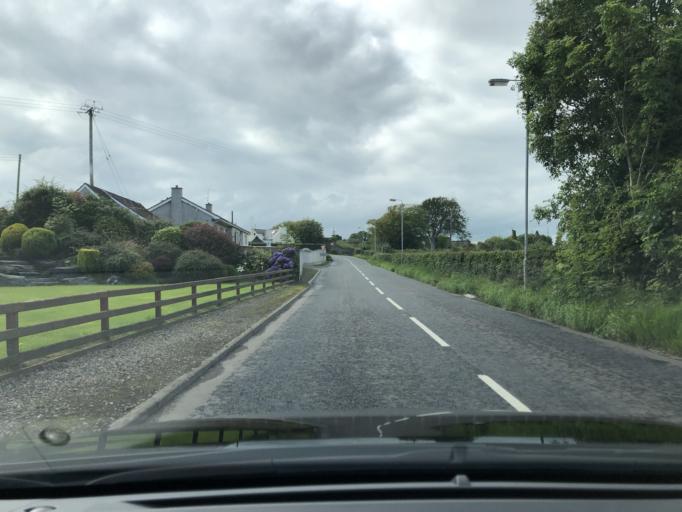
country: GB
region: Northern Ireland
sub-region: Down District
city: Dundrum
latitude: 54.2888
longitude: -5.8334
